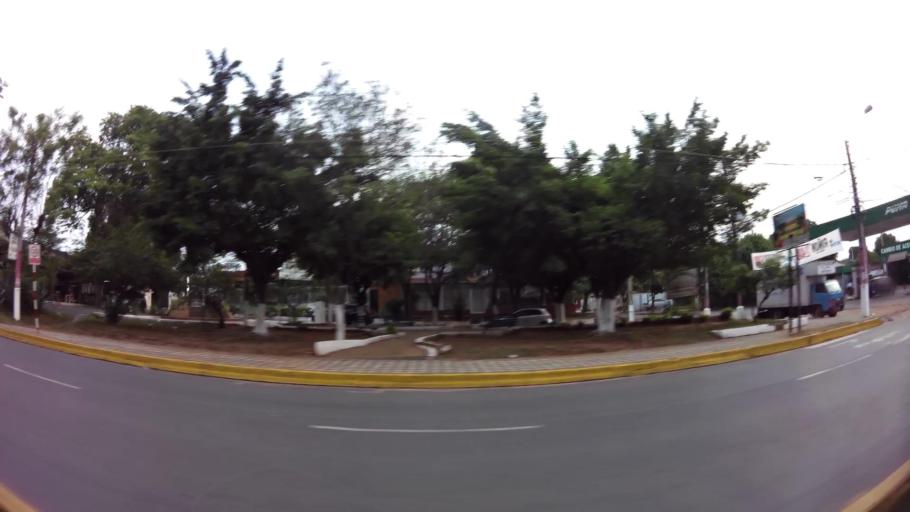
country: PY
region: Central
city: Lambare
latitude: -25.3437
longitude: -57.6176
